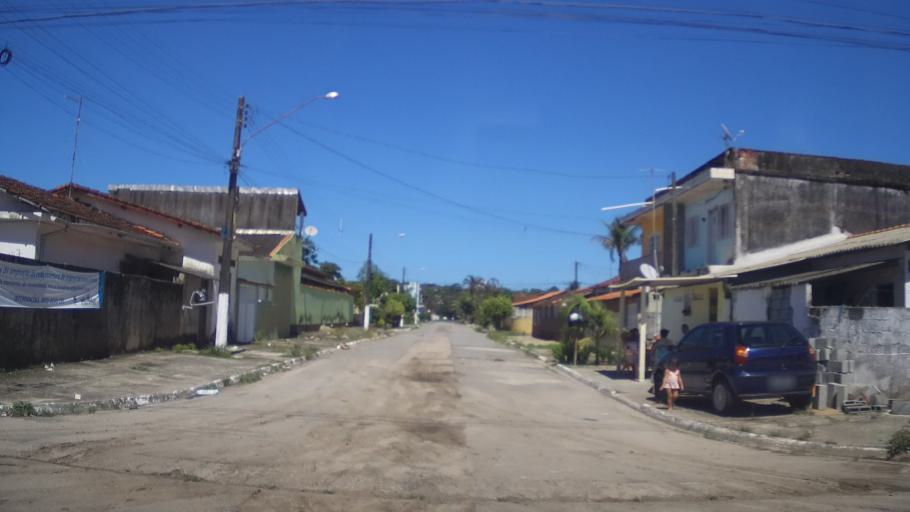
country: BR
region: Sao Paulo
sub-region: Mongagua
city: Mongagua
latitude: -24.0740
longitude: -46.5940
